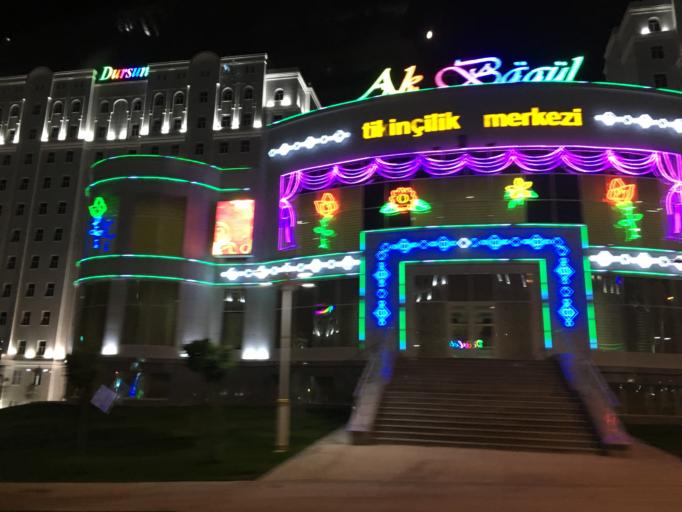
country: TM
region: Ahal
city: Ashgabat
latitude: 37.9409
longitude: 58.3480
